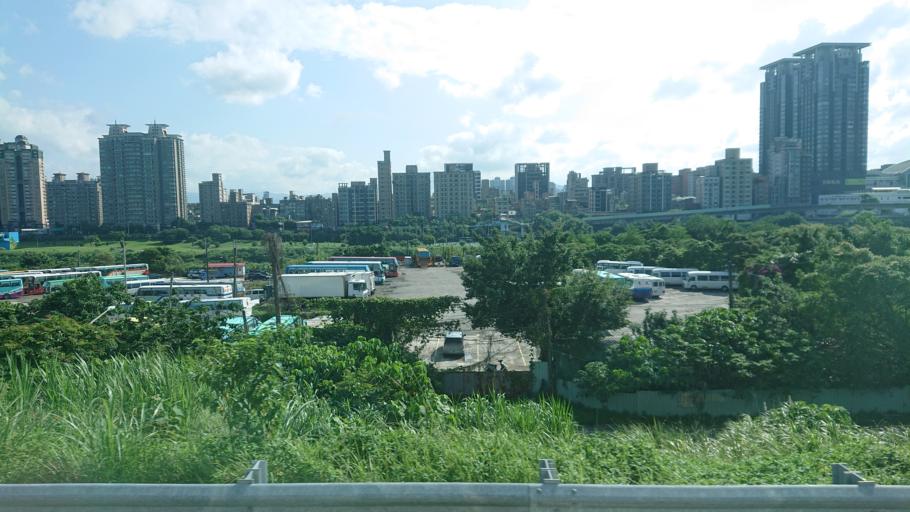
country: TW
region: Taipei
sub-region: Taipei
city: Banqiao
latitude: 24.9706
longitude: 121.5244
